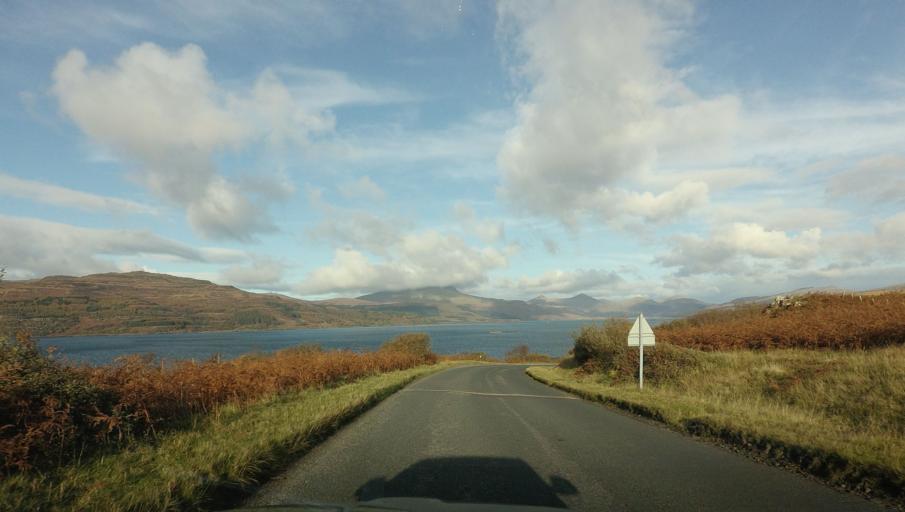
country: GB
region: Scotland
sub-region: Argyll and Bute
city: Isle Of Mull
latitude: 56.3430
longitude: -6.1226
